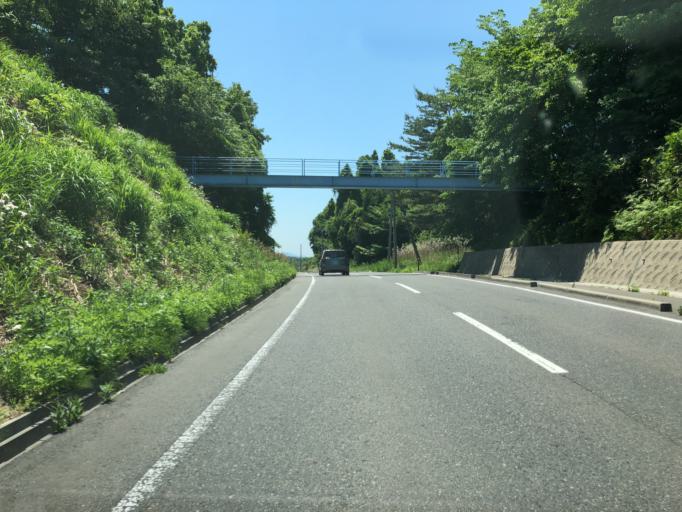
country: JP
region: Fukushima
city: Motomiya
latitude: 37.5166
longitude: 140.4584
